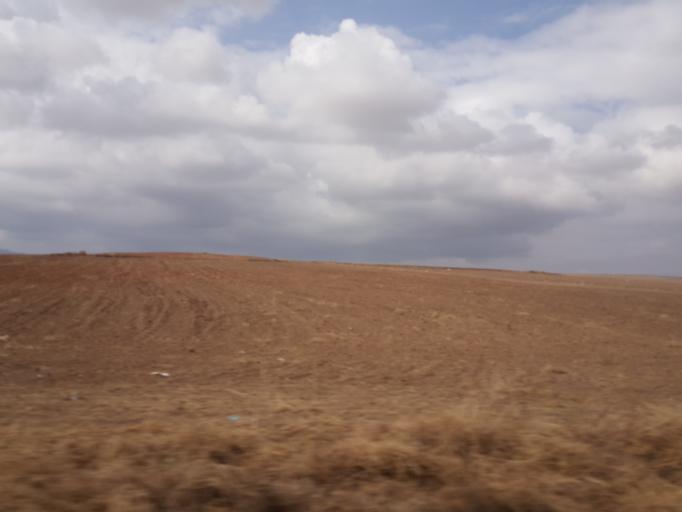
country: TR
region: Kirikkale
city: Keskin
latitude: 39.6097
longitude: 33.6133
